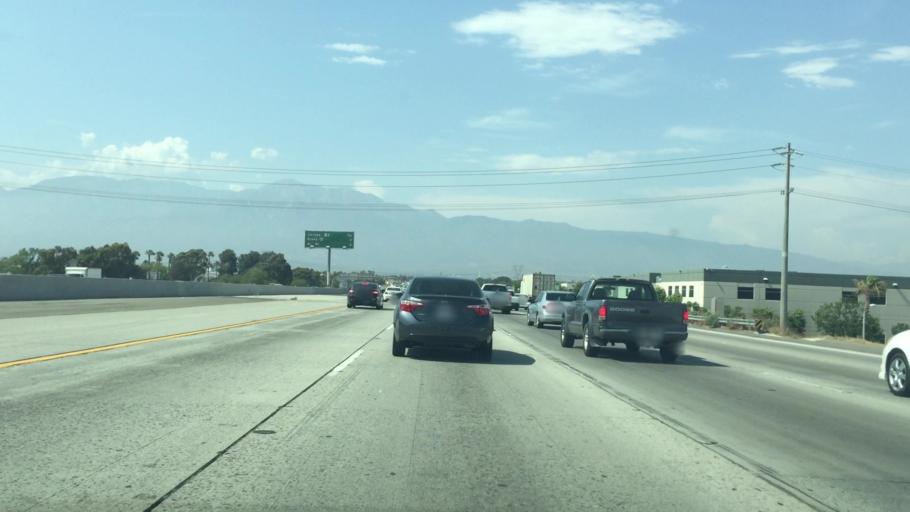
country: US
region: California
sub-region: Riverside County
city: Mira Loma
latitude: 34.0327
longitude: -117.5500
